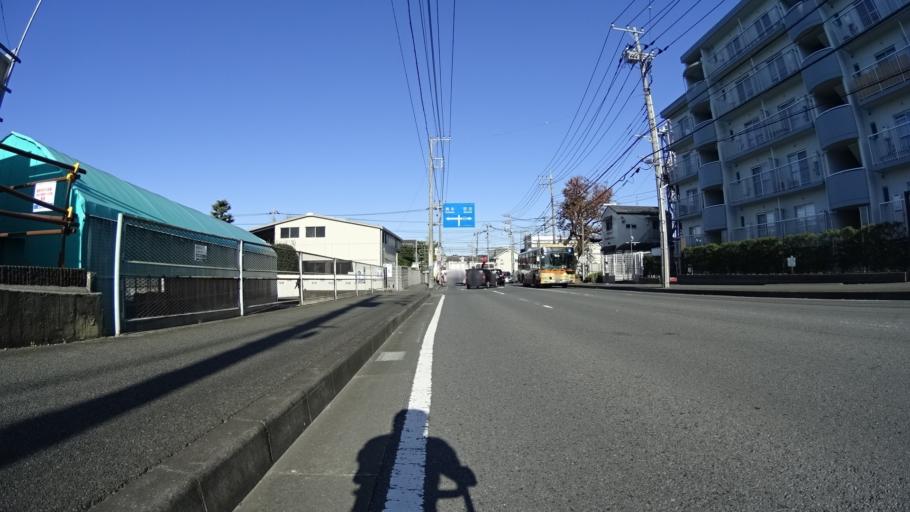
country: JP
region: Tokyo
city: Hachioji
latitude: 35.5913
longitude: 139.3680
